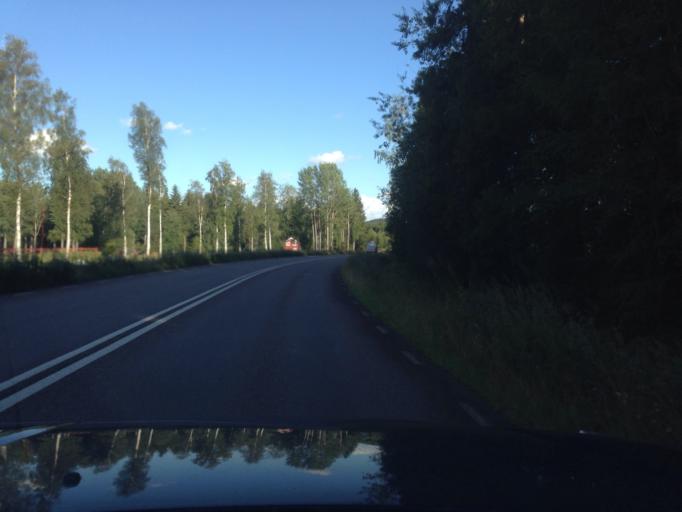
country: SE
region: Dalarna
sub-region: Ludvika Kommun
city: Ludvika
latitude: 60.1470
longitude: 15.1012
